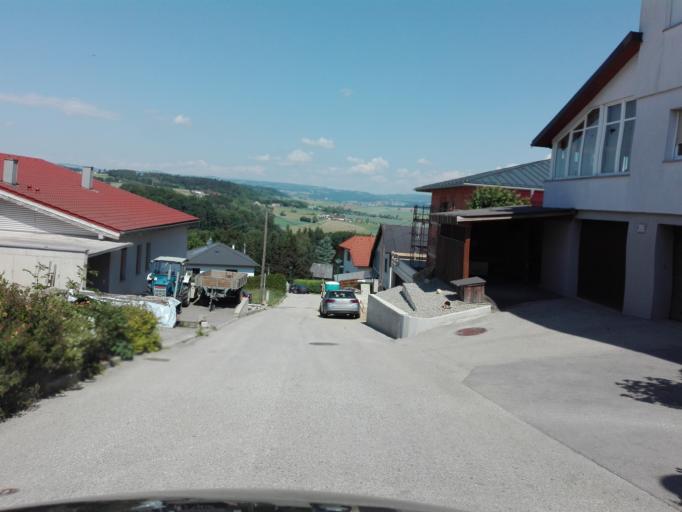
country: AT
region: Upper Austria
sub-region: Politischer Bezirk Urfahr-Umgebung
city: Engerwitzdorf
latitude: 48.2842
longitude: 14.4723
